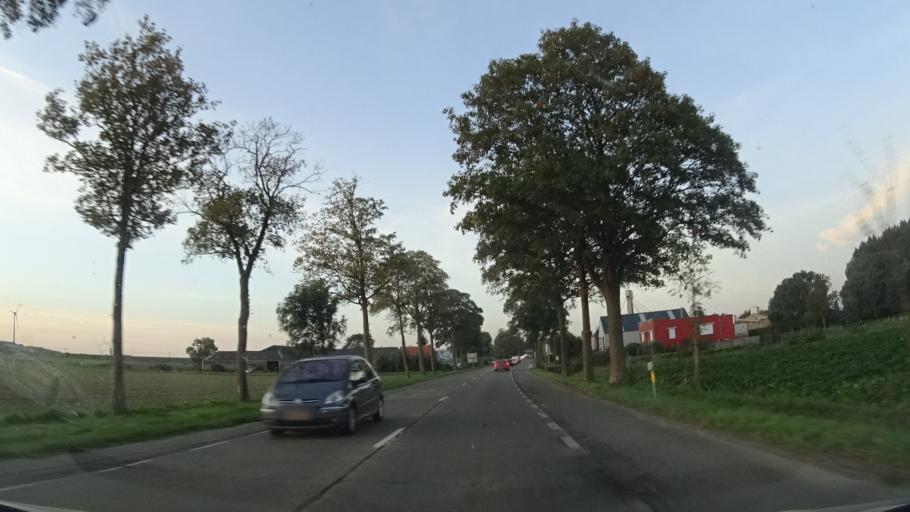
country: BE
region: Wallonia
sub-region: Province du Hainaut
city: Peruwelz
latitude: 50.5668
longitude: 3.6142
